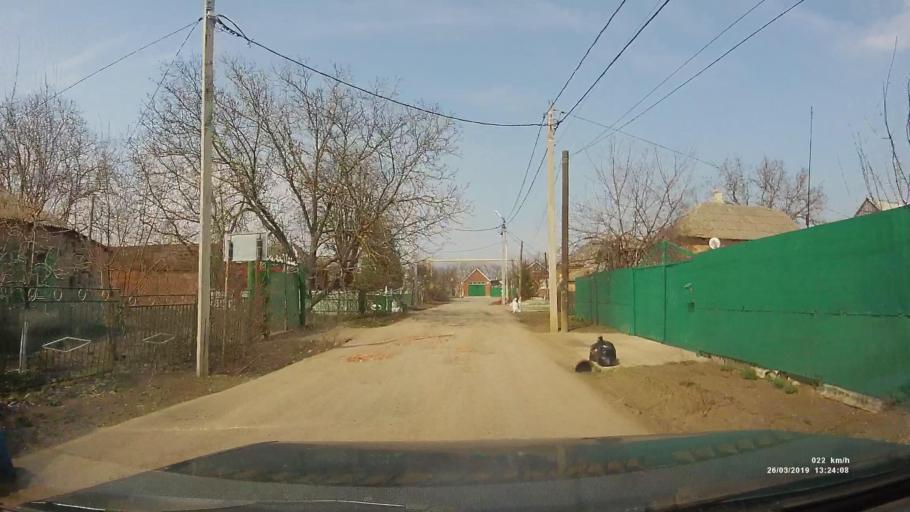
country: RU
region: Rostov
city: Novobessergenovka
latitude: 47.1742
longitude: 38.7660
